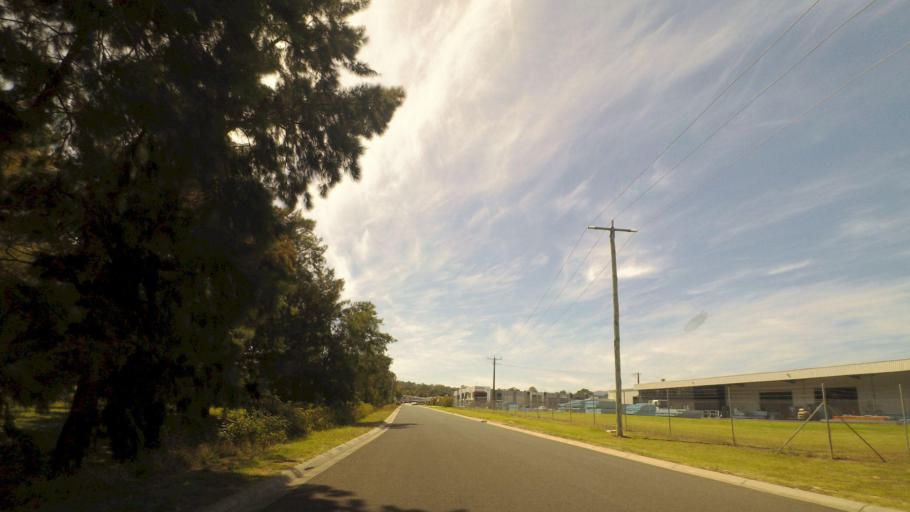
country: AU
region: Victoria
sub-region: Maroondah
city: Croydon North
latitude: -37.7696
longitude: 145.2993
